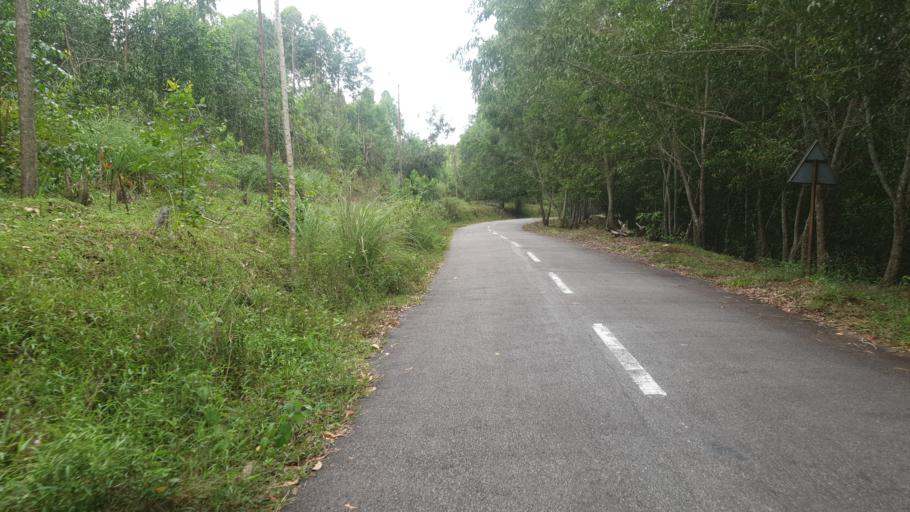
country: IN
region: Kerala
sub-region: Thiruvananthapuram
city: Nedumangad
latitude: 8.6338
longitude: 77.1123
